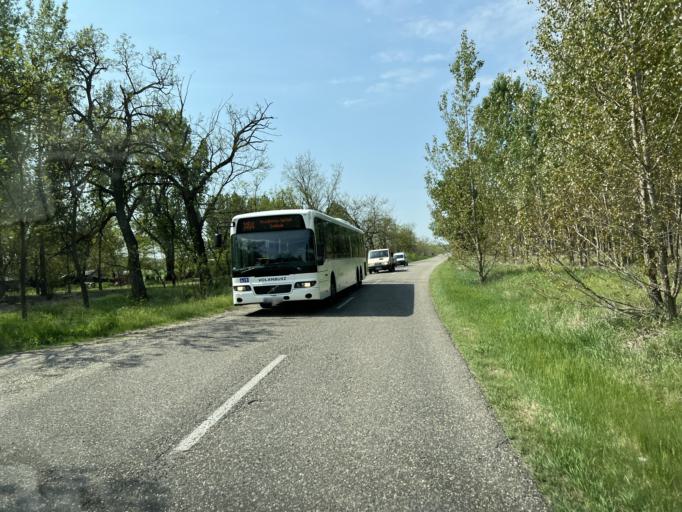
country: HU
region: Pest
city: Kocser
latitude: 47.0629
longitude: 19.8613
